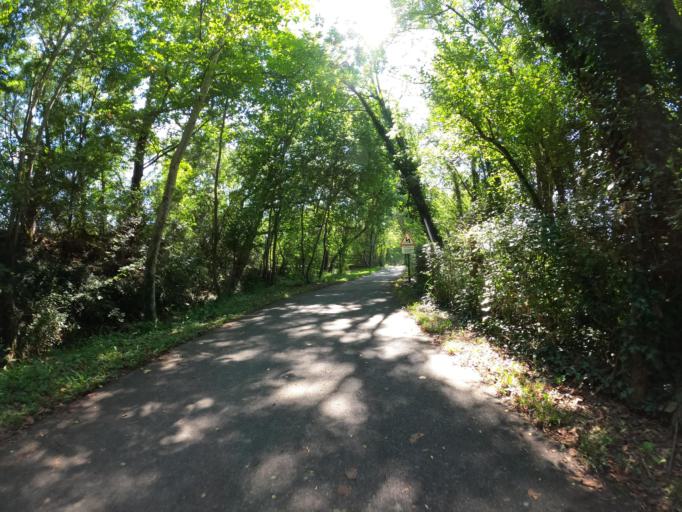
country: FR
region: Aquitaine
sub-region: Departement du Lot-et-Garonne
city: Bias
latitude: 44.4072
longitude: 0.6634
